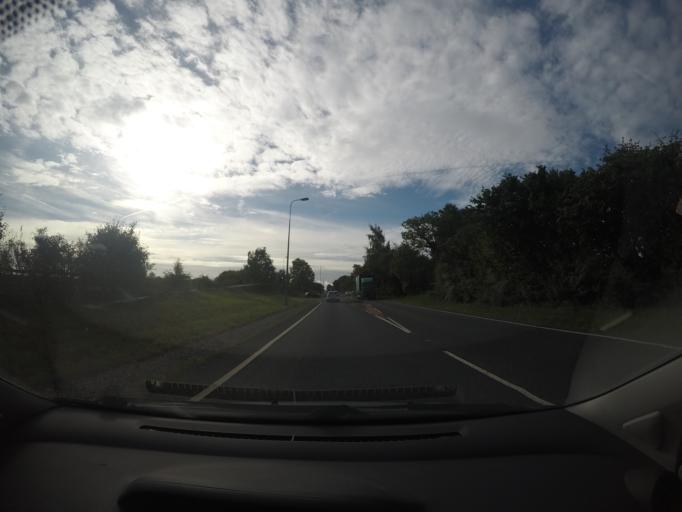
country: GB
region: England
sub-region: North Yorkshire
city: Riccall
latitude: 53.8317
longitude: -1.0530
